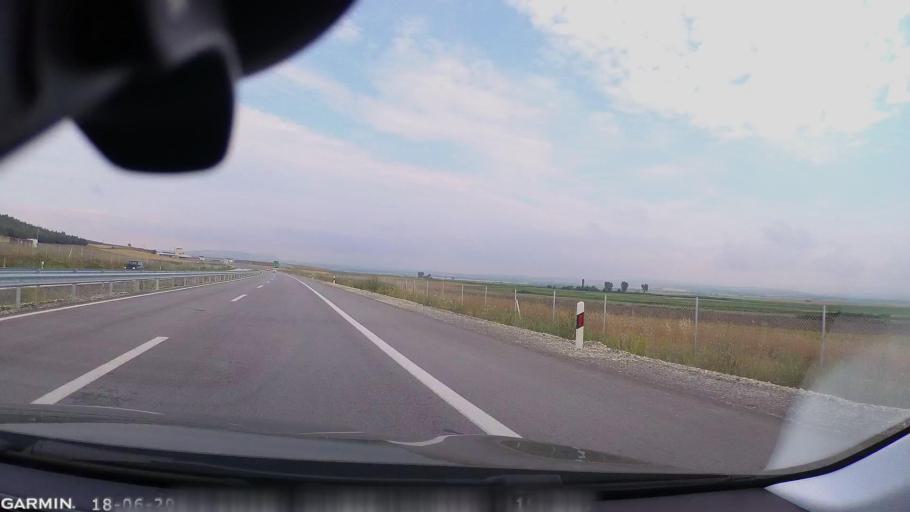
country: MK
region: Sveti Nikole
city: Sveti Nikole
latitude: 41.8085
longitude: 22.0599
